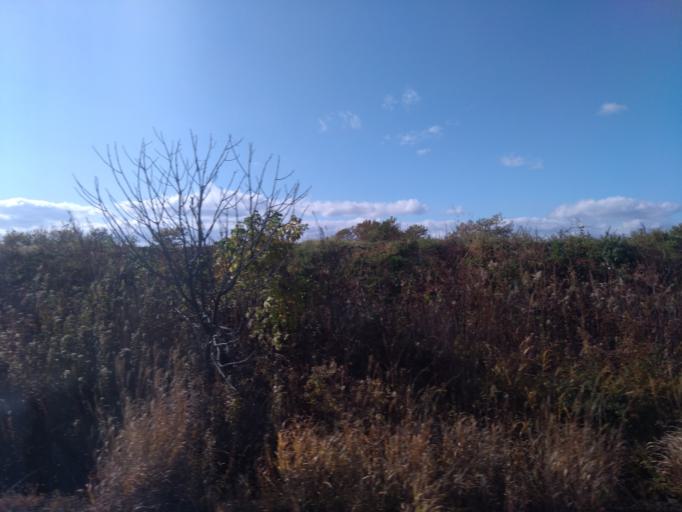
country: JP
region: Hokkaido
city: Kitahiroshima
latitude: 42.9341
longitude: 141.5724
